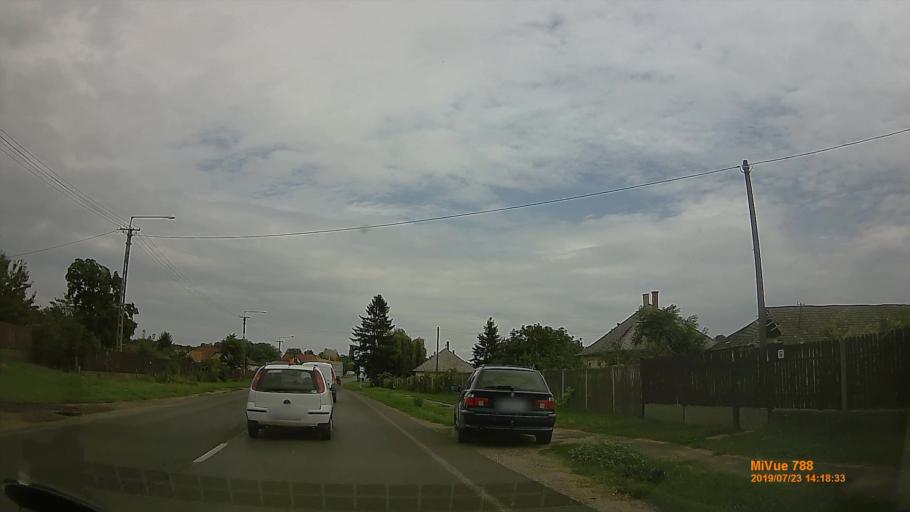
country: HU
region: Szabolcs-Szatmar-Bereg
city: Nagycserkesz
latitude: 47.9619
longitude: 21.5650
